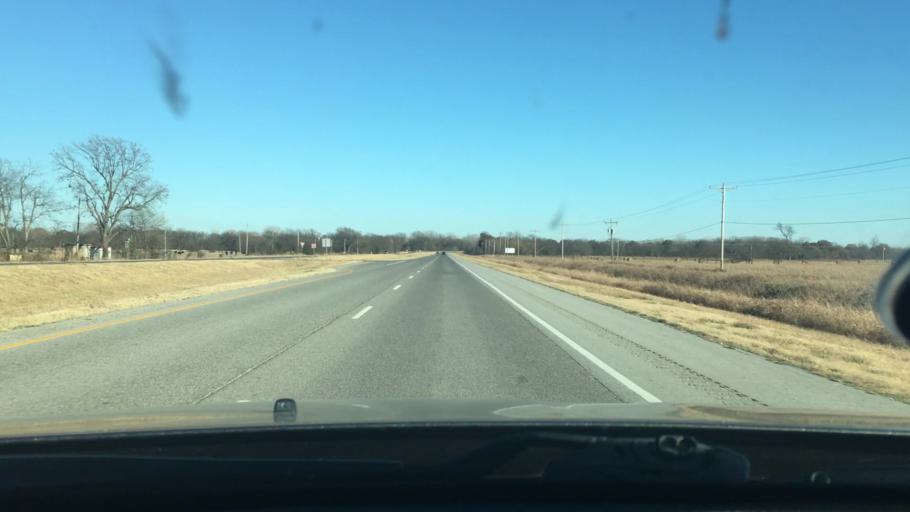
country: US
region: Oklahoma
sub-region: Murray County
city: Davis
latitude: 34.5064
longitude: -97.1613
